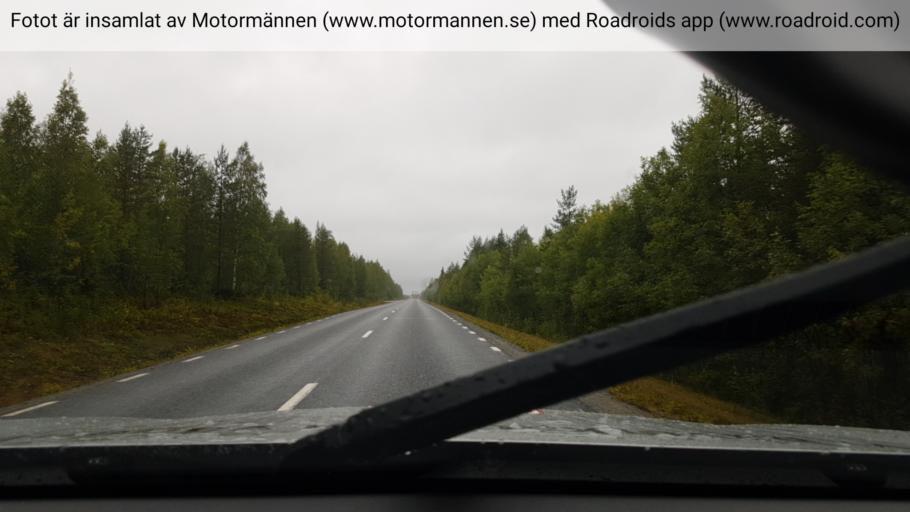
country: SE
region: Vaesterbotten
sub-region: Lycksele Kommun
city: Lycksele
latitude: 64.0593
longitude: 18.5082
